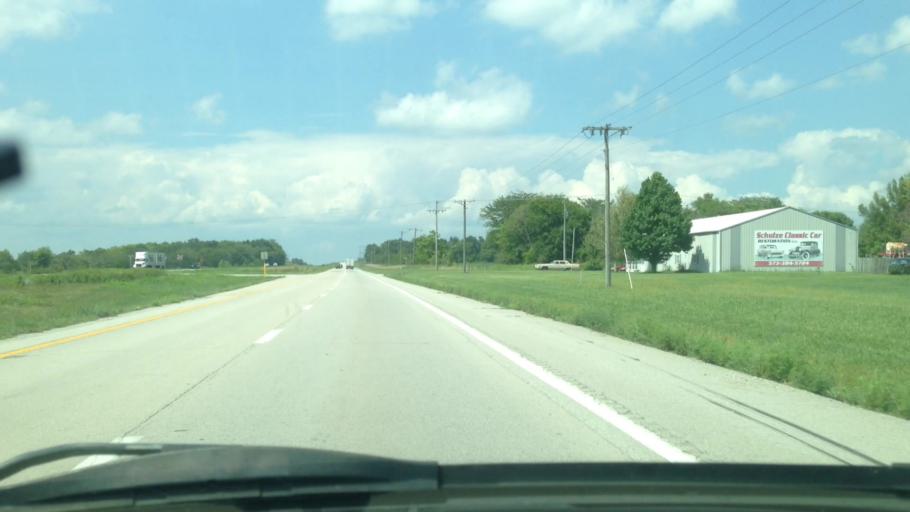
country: US
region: Missouri
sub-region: Lincoln County
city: Troy
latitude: 39.1402
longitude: -90.9654
